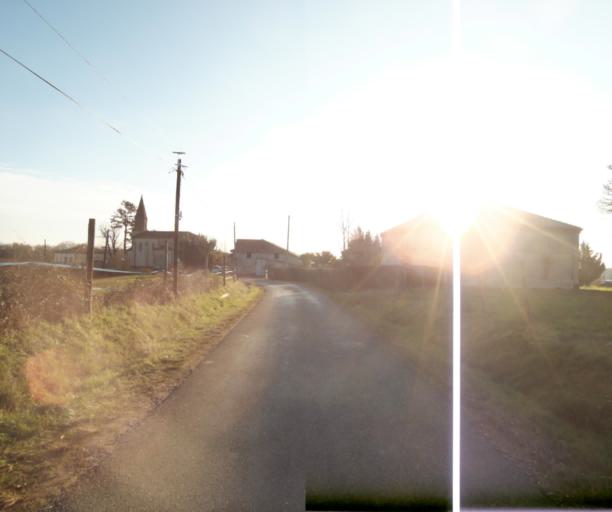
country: FR
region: Midi-Pyrenees
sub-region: Departement du Tarn-et-Garonne
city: Moissac
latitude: 44.1487
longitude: 1.1408
